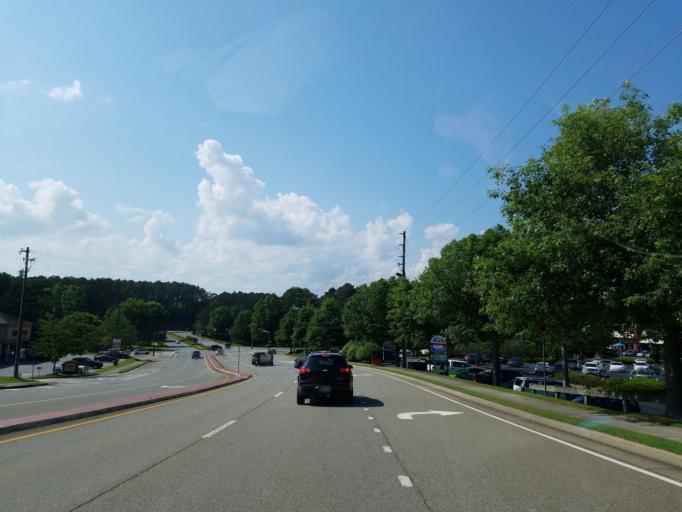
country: US
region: Georgia
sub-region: Cherokee County
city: Holly Springs
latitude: 34.1781
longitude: -84.5499
